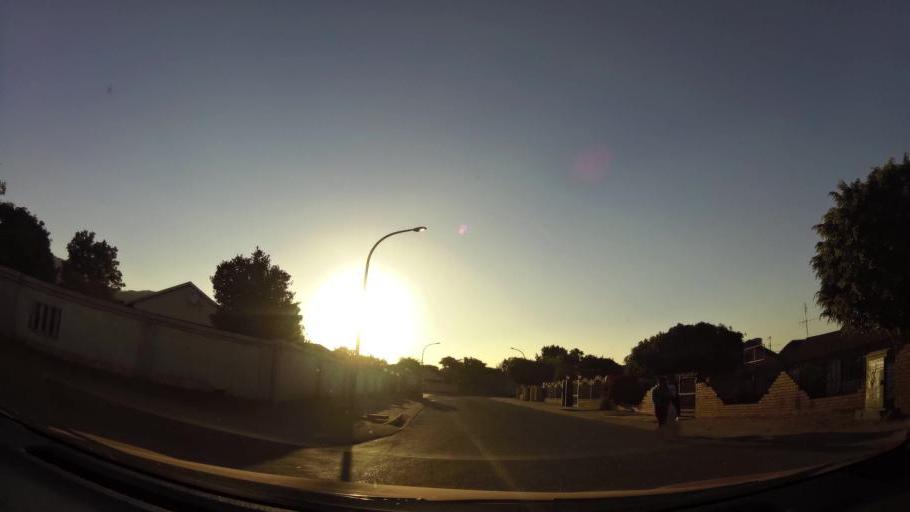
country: ZA
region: North-West
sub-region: Bojanala Platinum District Municipality
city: Rustenburg
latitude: -25.6421
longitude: 27.2087
